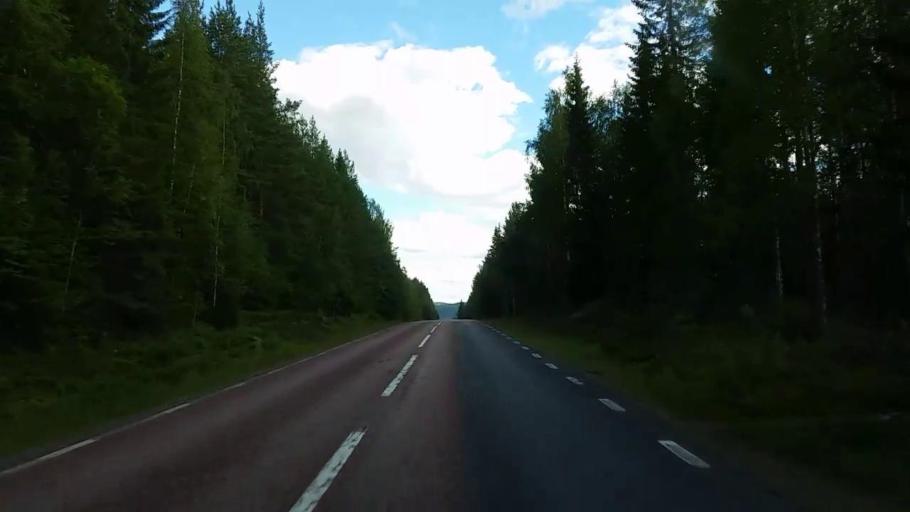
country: SE
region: Gaevleborg
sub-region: Ljusdals Kommun
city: Farila
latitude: 62.1436
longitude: 15.6864
